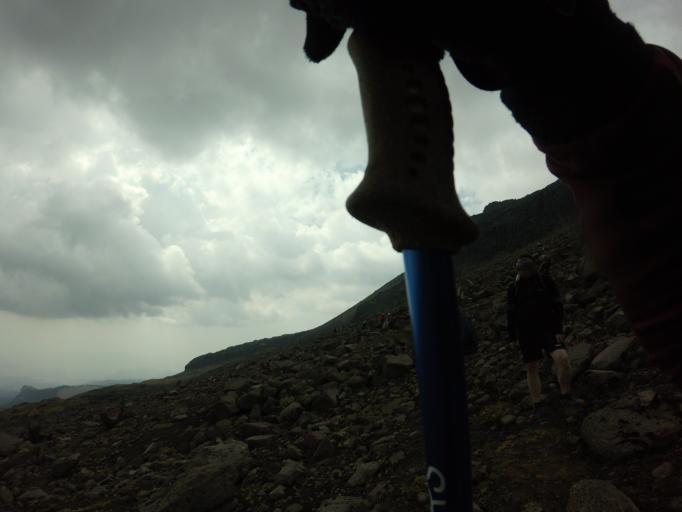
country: MX
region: Mexico
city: Amecameca de Juarez
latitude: 19.1565
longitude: -98.6423
